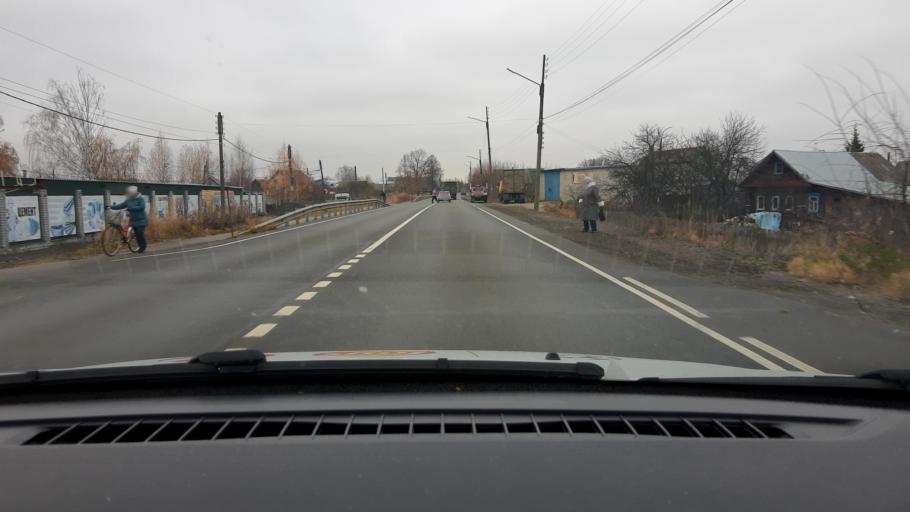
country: RU
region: Nizjnij Novgorod
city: Gidrotorf
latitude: 56.5332
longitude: 43.5411
